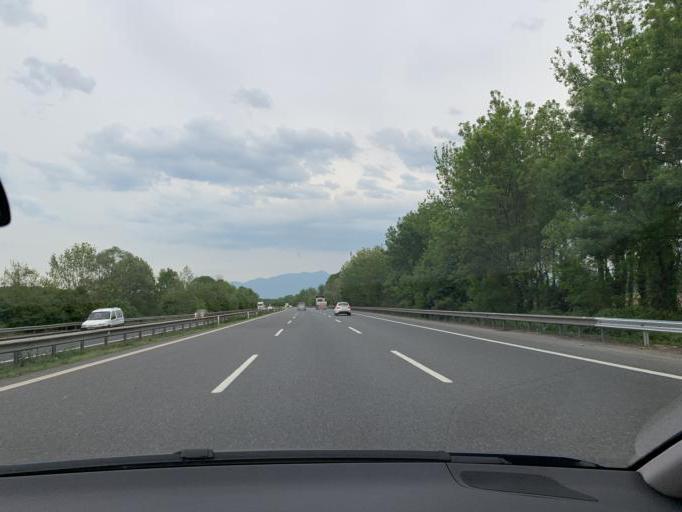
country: TR
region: Sakarya
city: Karapurcek
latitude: 40.7133
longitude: 30.4966
